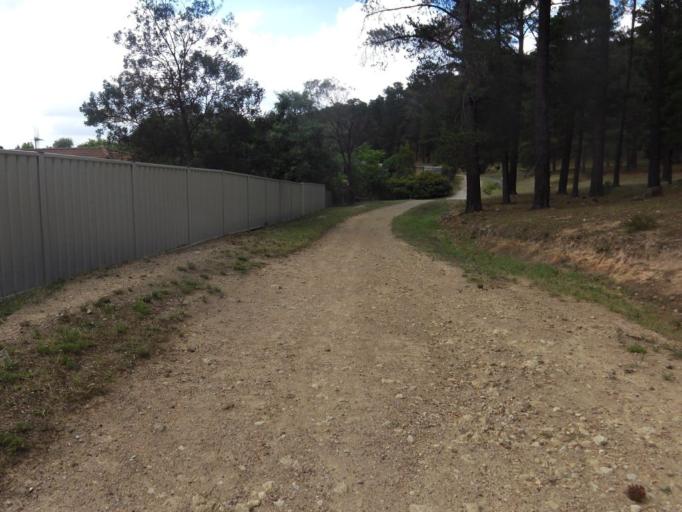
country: AU
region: Australian Capital Territory
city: Macarthur
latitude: -35.3697
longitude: 149.1161
